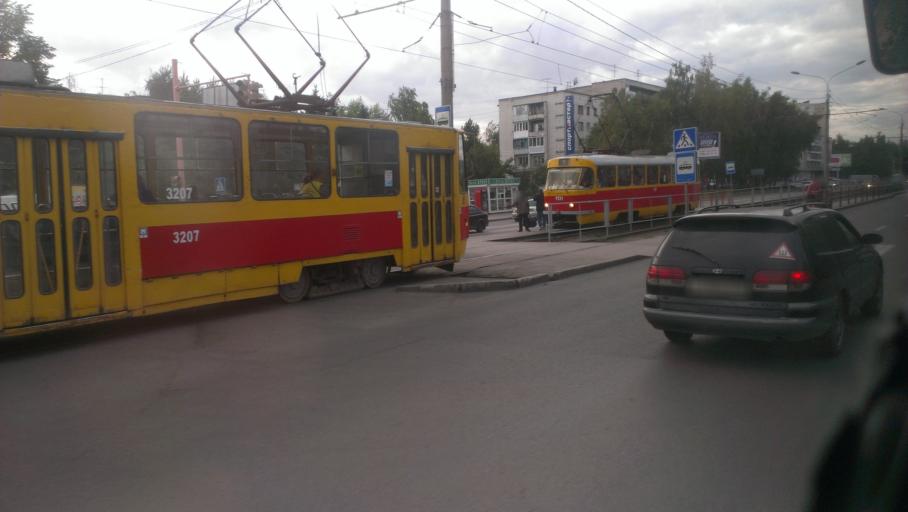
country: RU
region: Altai Krai
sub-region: Gorod Barnaulskiy
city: Barnaul
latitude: 53.3448
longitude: 83.7663
